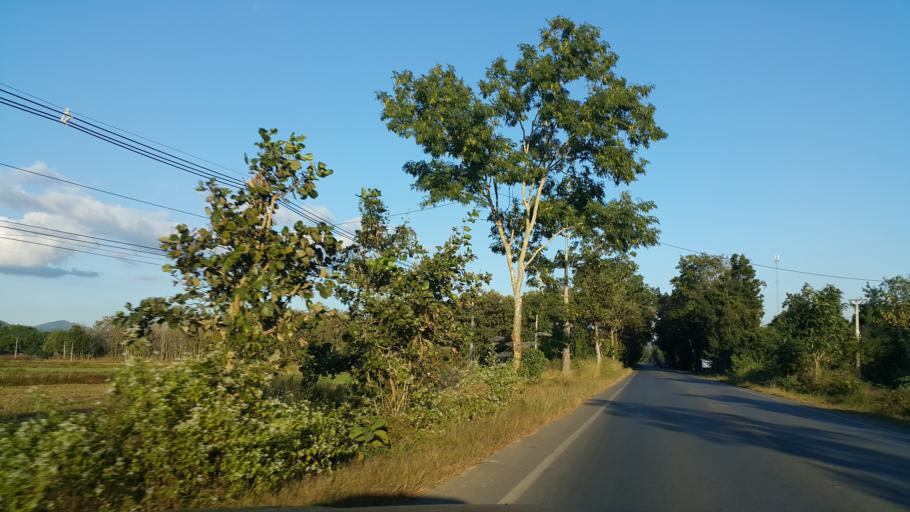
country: TH
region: Sukhothai
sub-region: Amphoe Si Satchanalai
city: Si Satchanalai
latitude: 17.5482
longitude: 99.8510
